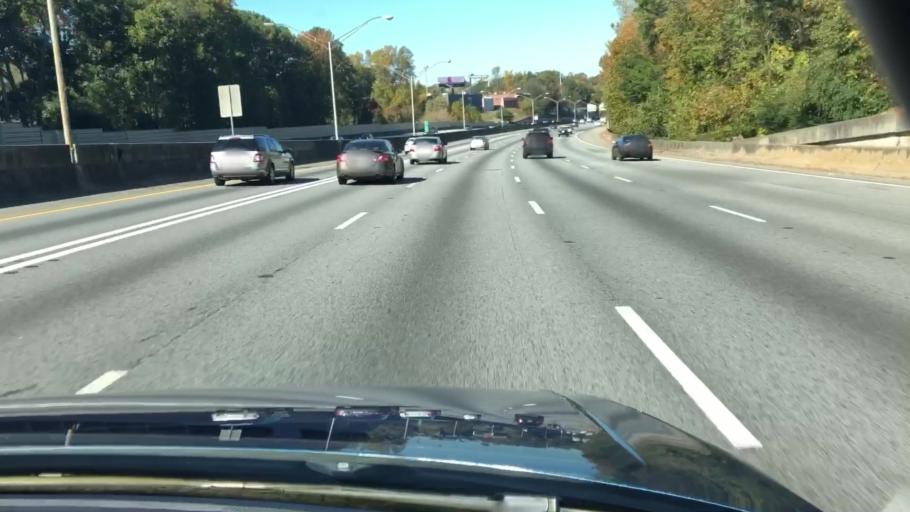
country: US
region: Georgia
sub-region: Fulton County
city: Atlanta
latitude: 33.8085
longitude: -84.4175
